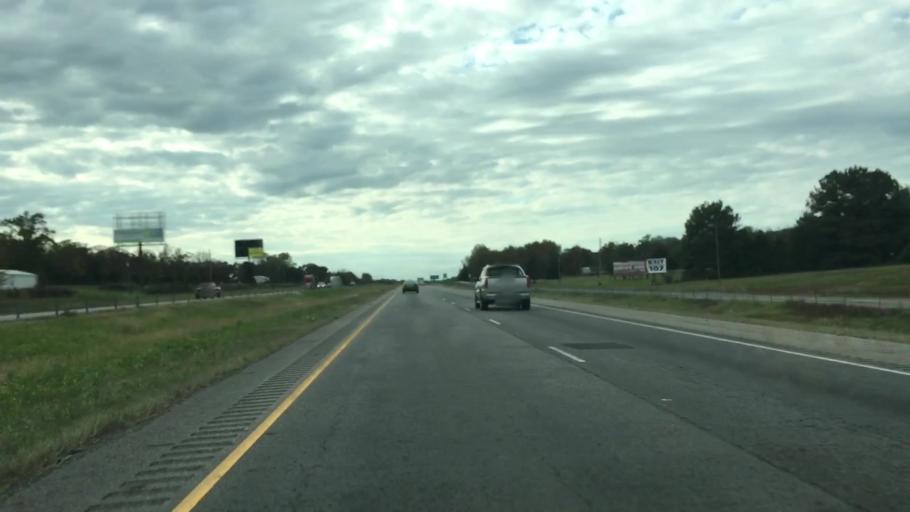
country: US
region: Arkansas
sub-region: Conway County
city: Morrilton
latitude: 35.1629
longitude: -92.6500
